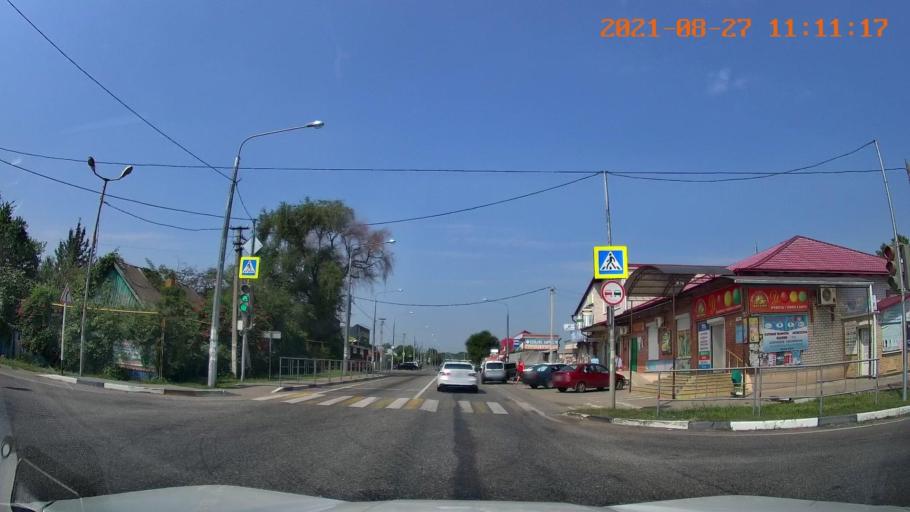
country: RU
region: Stavropol'skiy
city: Ivanovskoye
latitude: 44.5717
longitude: 41.8715
